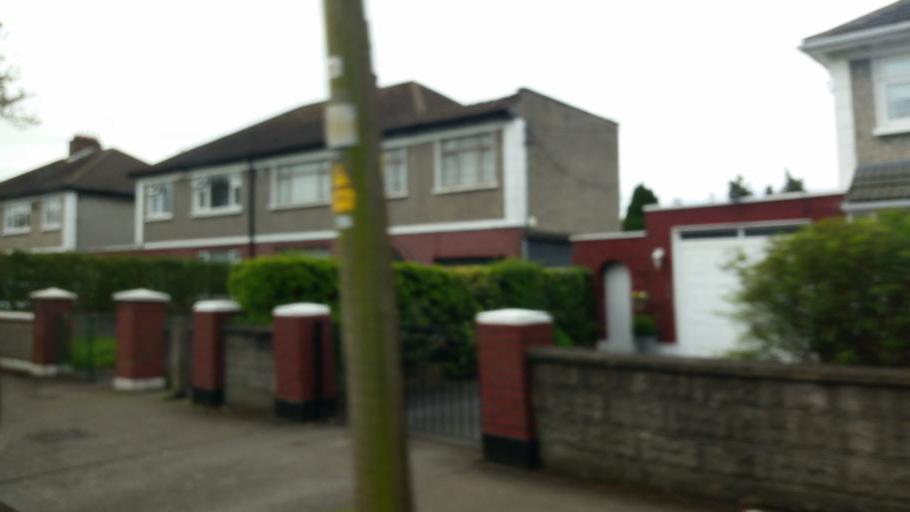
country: IE
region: Leinster
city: Ballymun
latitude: 53.3910
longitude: -6.2742
